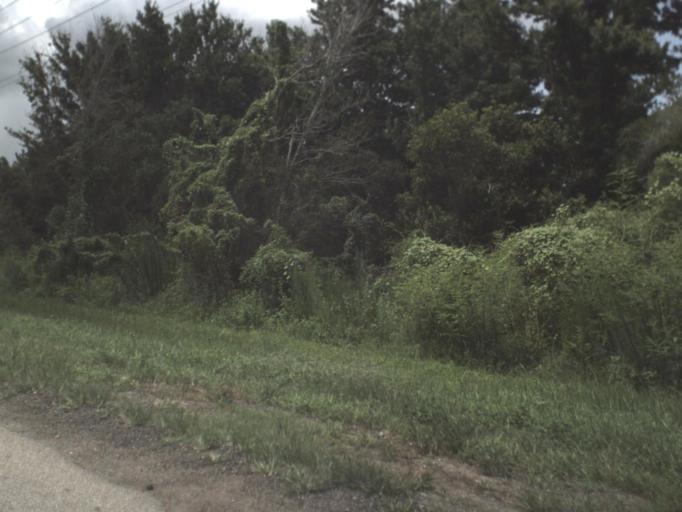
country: US
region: Florida
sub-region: Hillsborough County
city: Sun City Center
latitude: 27.7485
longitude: -82.3352
